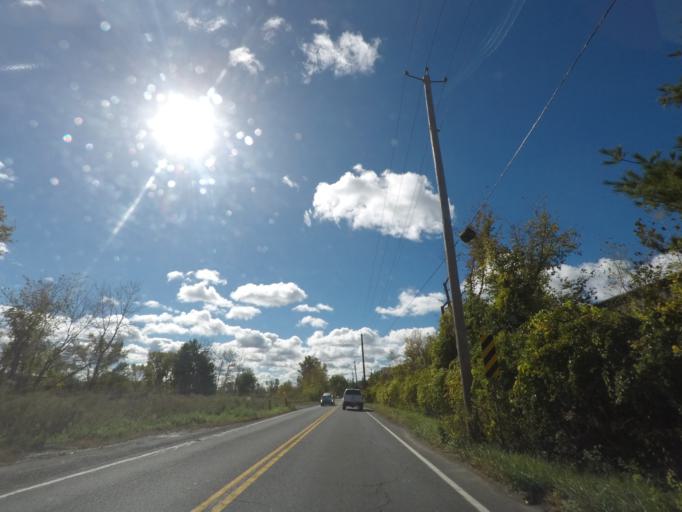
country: US
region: New York
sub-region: Albany County
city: Menands
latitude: 42.7130
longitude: -73.7194
